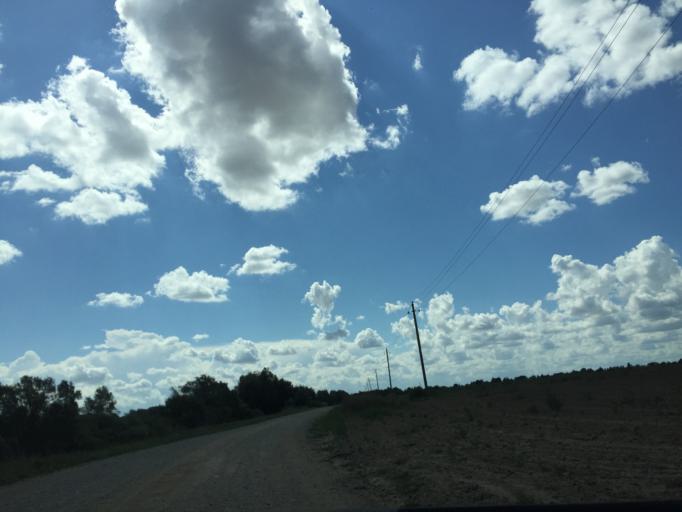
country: LV
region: Rundales
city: Pilsrundale
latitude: 56.2858
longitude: 23.9965
